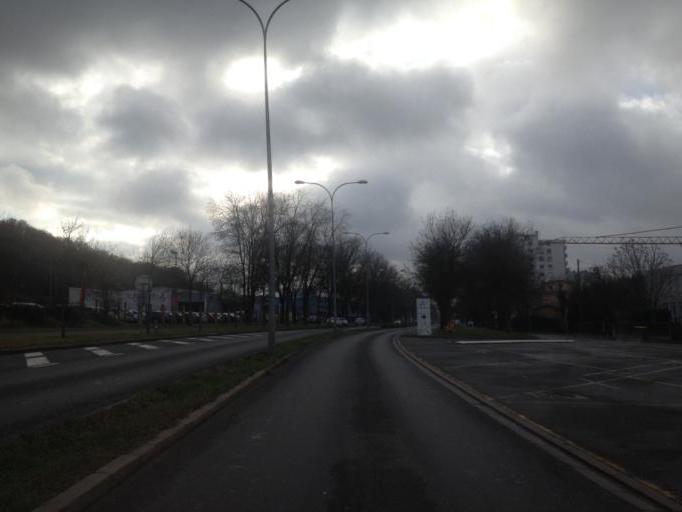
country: FR
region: Auvergne
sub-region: Departement de l'Allier
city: Creuzier-le-Vieux
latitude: 46.1491
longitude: 3.4141
